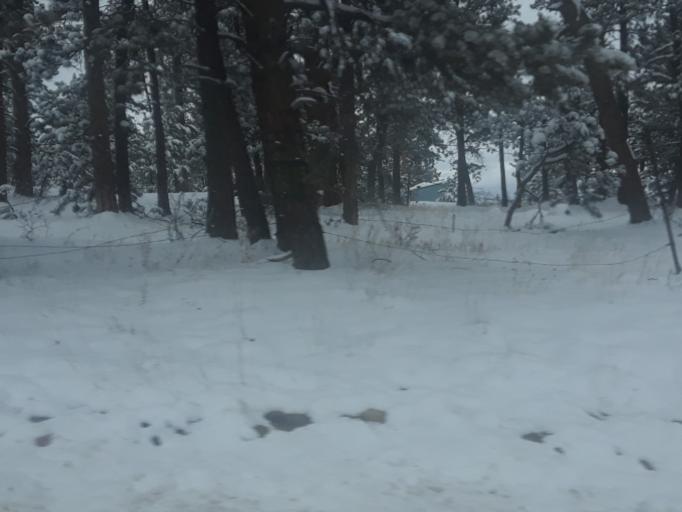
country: US
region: Colorado
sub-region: Boulder County
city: Coal Creek
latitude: 39.9205
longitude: -105.3661
